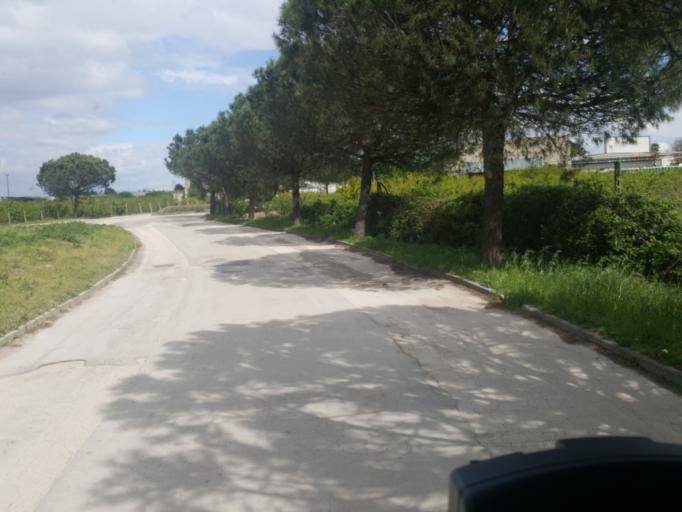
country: IT
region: Campania
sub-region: Provincia di Napoli
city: Torretta-Scalzapecora
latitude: 40.9346
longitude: 14.1136
